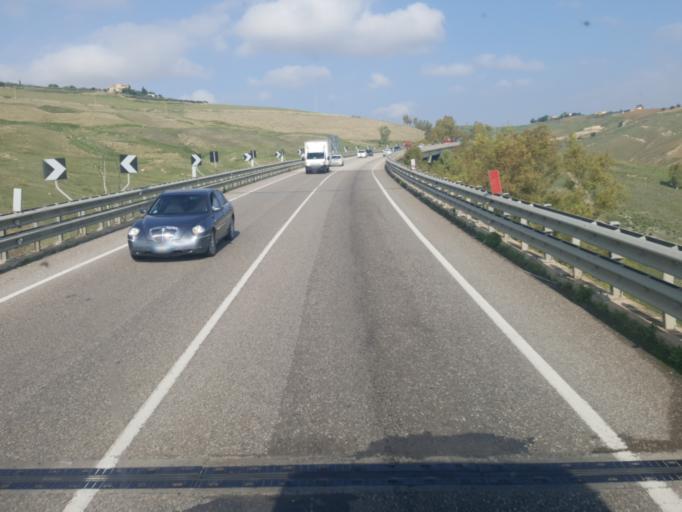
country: IT
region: Sicily
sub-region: Provincia di Caltanissetta
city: Caltanissetta
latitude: 37.4647
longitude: 14.1001
